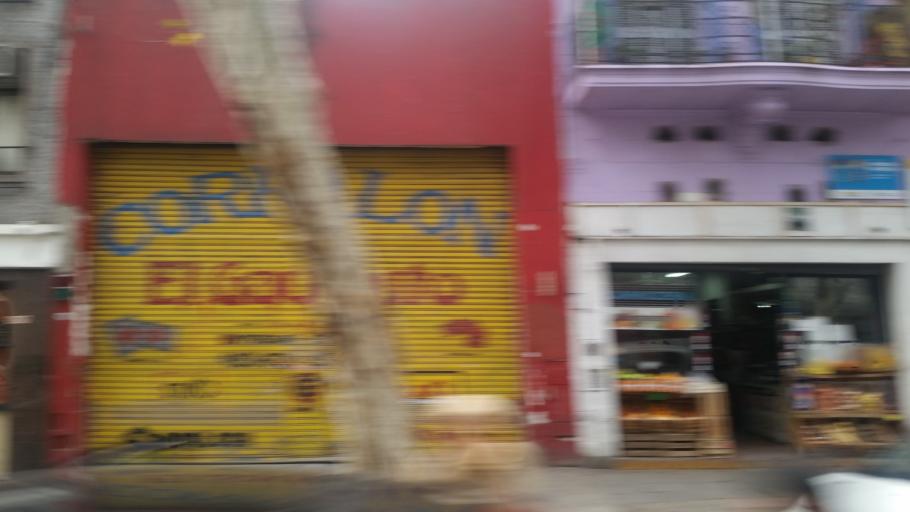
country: AR
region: Buenos Aires F.D.
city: Buenos Aires
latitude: -34.6061
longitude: -58.3976
